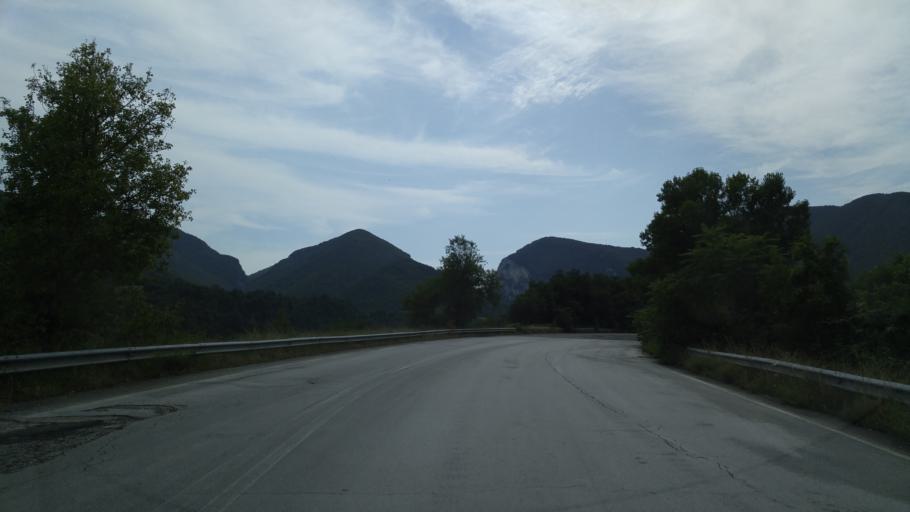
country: IT
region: The Marches
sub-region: Provincia di Pesaro e Urbino
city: Canavaccio
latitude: 43.6654
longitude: 12.7541
